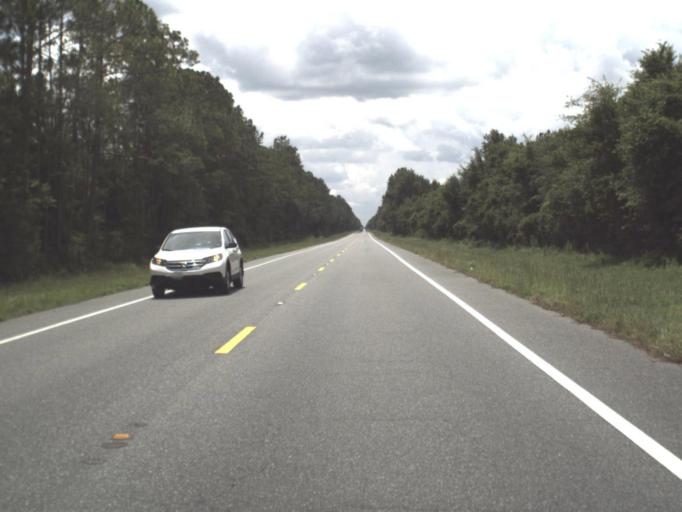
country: US
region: Florida
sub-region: Columbia County
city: Watertown
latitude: 30.1446
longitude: -82.5440
